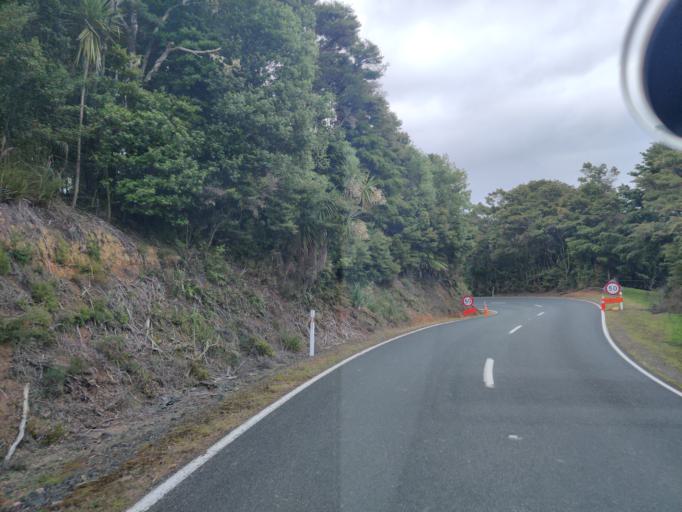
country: NZ
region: Northland
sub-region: Whangarei
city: Ngunguru
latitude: -35.5776
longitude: 174.4073
